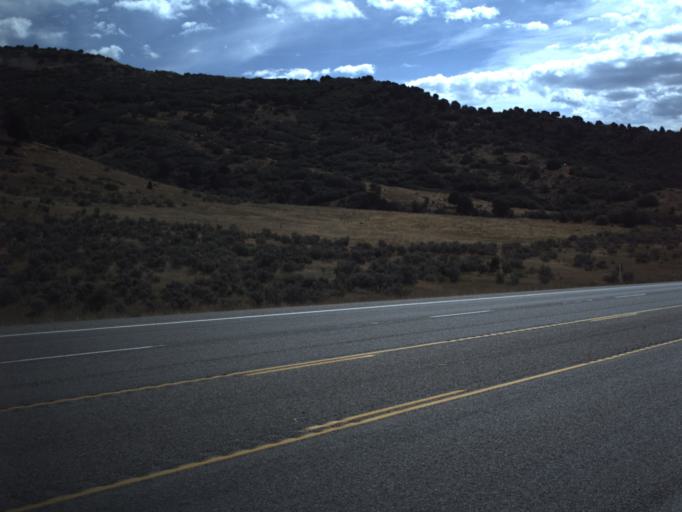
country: US
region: Utah
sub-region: Utah County
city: Mapleton
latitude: 40.0000
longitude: -111.4812
